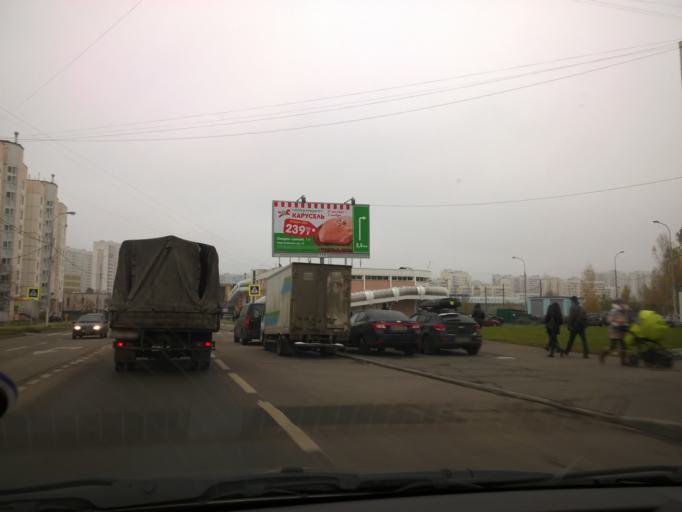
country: RU
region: Moskovskaya
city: Kommunarka
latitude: 55.5344
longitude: 37.5164
